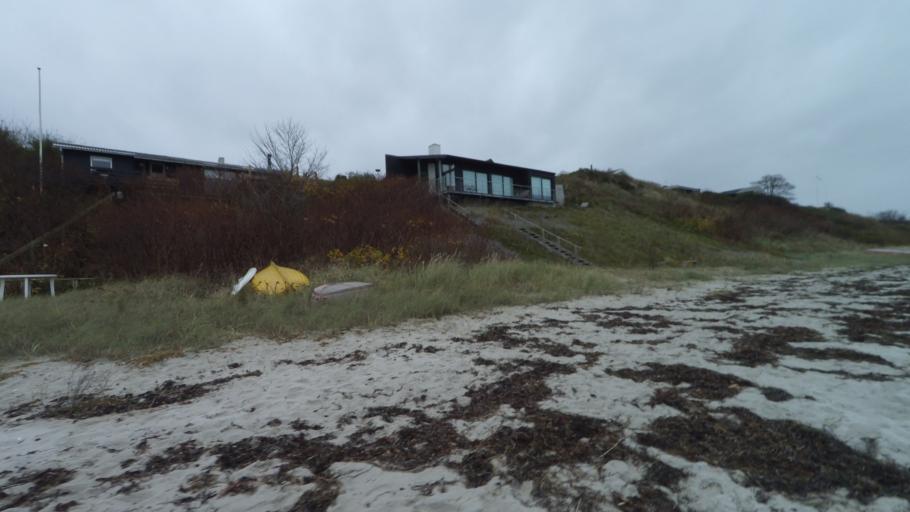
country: DK
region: Central Jutland
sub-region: Arhus Kommune
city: Malling
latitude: 55.9871
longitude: 10.2526
